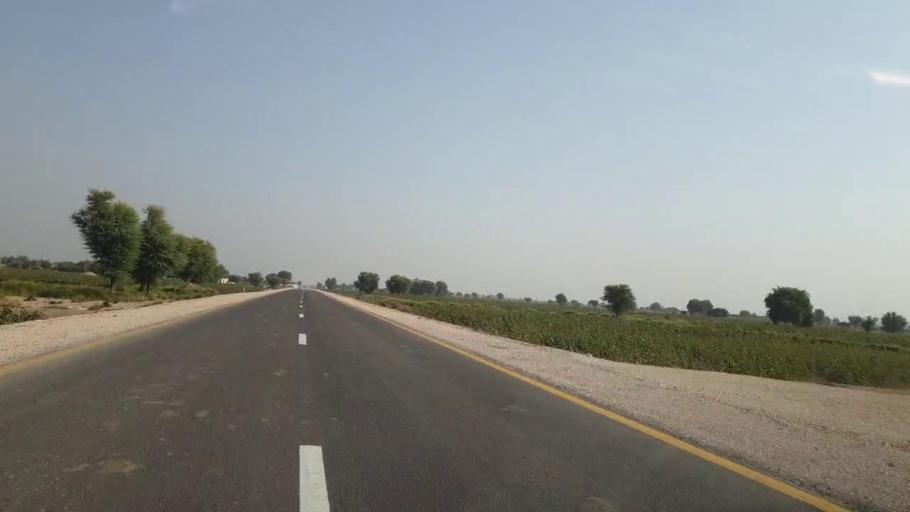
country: PK
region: Sindh
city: Sehwan
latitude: 26.4747
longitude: 67.7881
